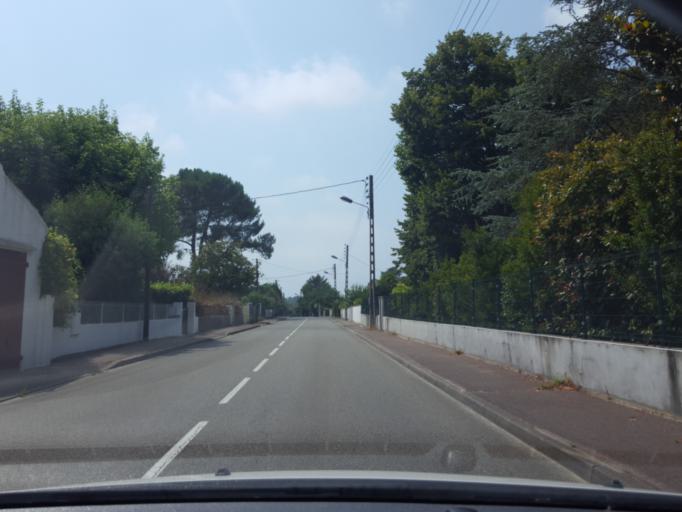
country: FR
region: Aquitaine
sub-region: Departement des Landes
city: Ondres
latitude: 43.5674
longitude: -1.4462
